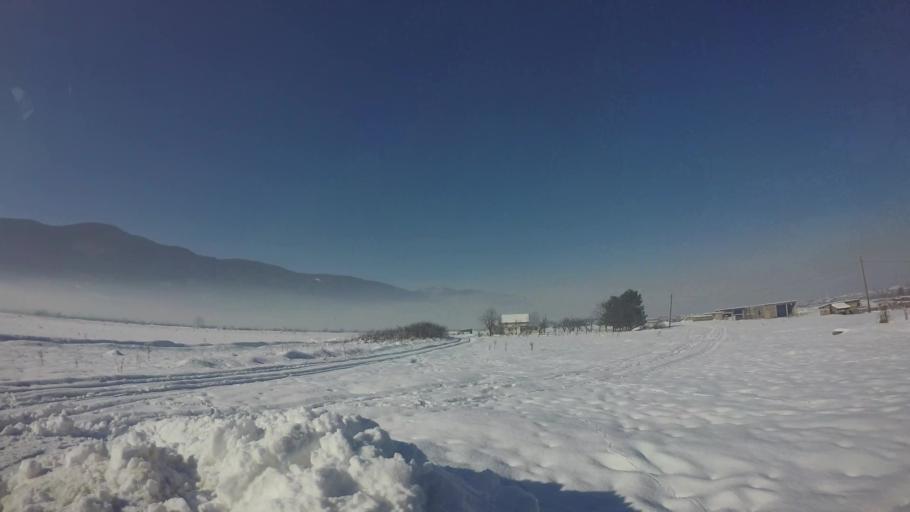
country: BA
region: Federation of Bosnia and Herzegovina
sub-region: Kanton Sarajevo
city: Sarajevo
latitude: 43.7997
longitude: 18.3341
